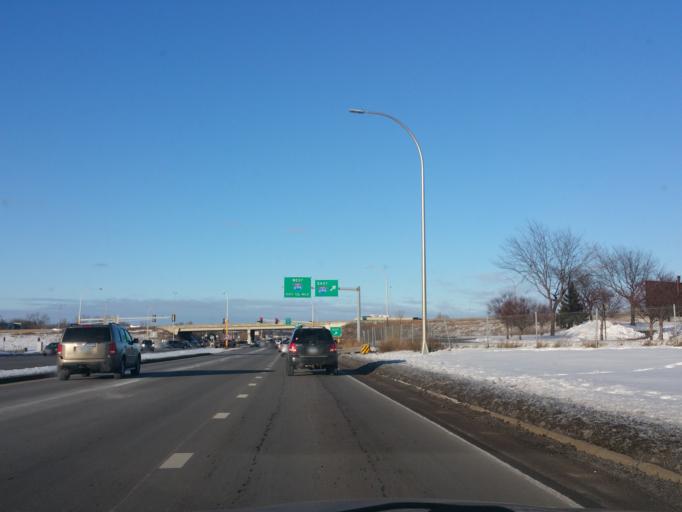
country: US
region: Minnesota
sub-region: Anoka County
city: Fridley
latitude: 45.0647
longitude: -93.2474
